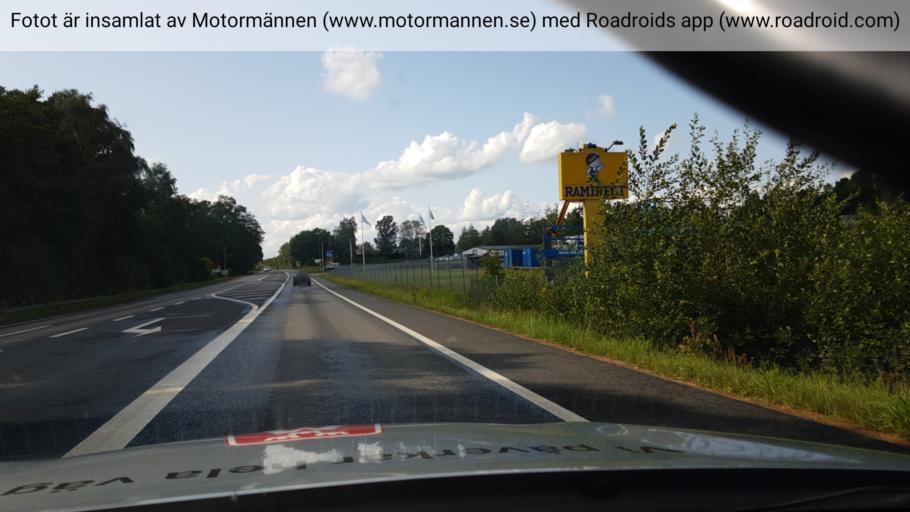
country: SE
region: Skane
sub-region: Hassleholms Kommun
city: Hassleholm
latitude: 56.1440
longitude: 13.7964
